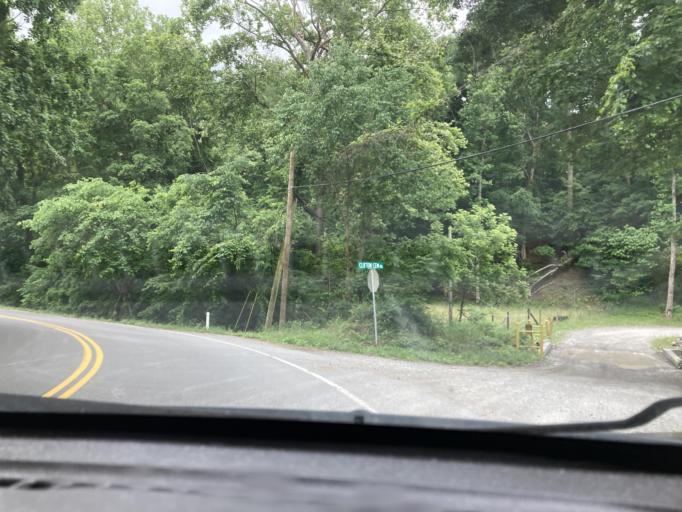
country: US
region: Tennessee
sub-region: Dickson County
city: Dickson
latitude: 36.0413
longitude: -87.3684
